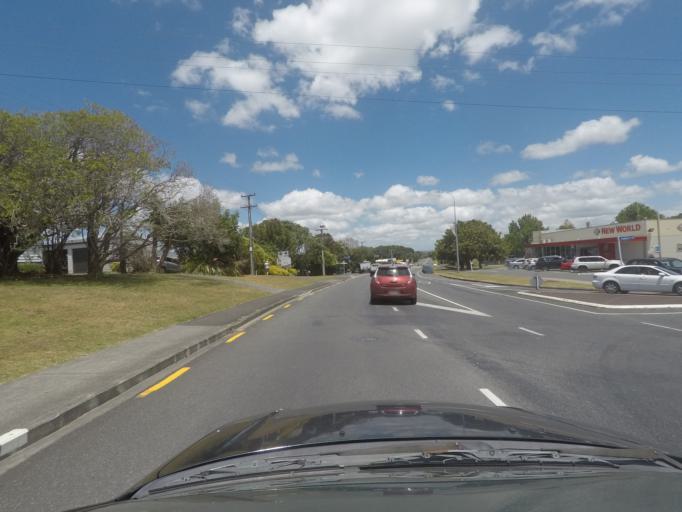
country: NZ
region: Northland
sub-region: Whangarei
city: Whangarei
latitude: -35.7555
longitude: 174.3686
